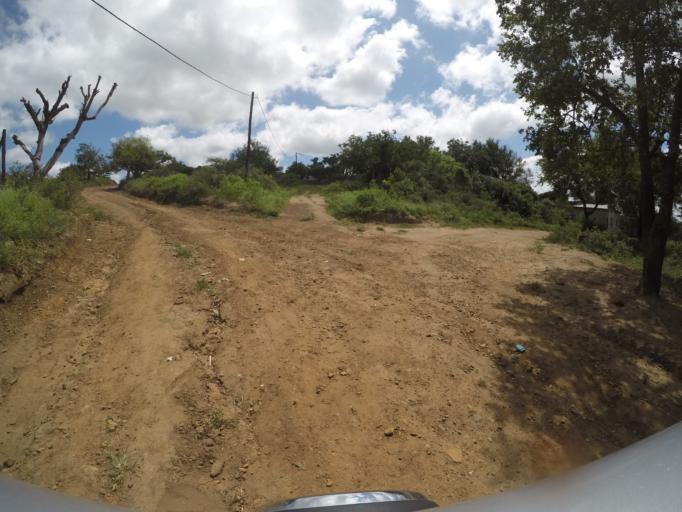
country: ZA
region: KwaZulu-Natal
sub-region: uThungulu District Municipality
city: Empangeni
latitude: -28.5844
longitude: 31.8376
